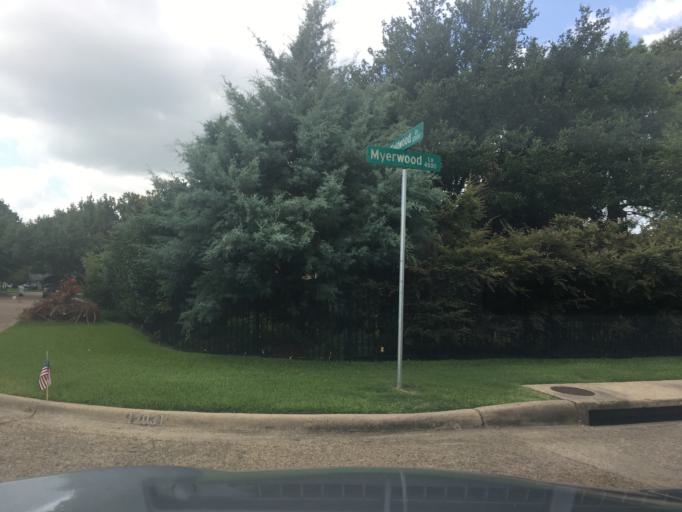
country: US
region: Texas
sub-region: Dallas County
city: Addison
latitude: 32.9140
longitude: -96.8247
